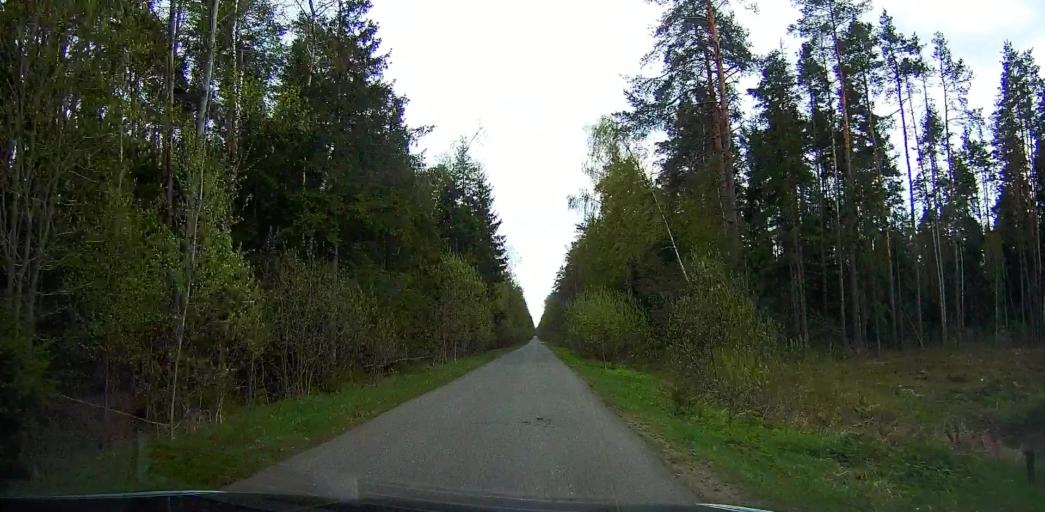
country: RU
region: Moskovskaya
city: Malyshevo
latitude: 55.5488
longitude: 38.3613
